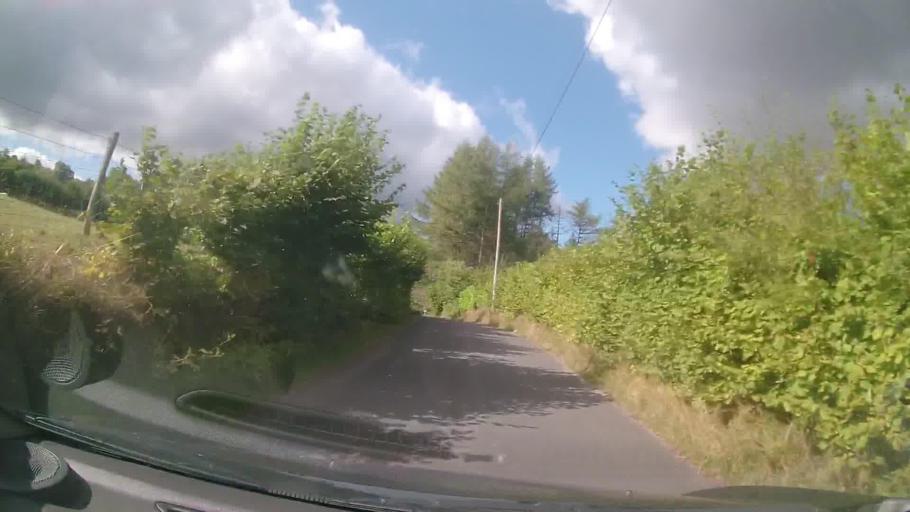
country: GB
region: Wales
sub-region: Merthyr Tydfil County Borough
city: Merthyr Tydfil
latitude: 51.8205
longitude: -3.3744
